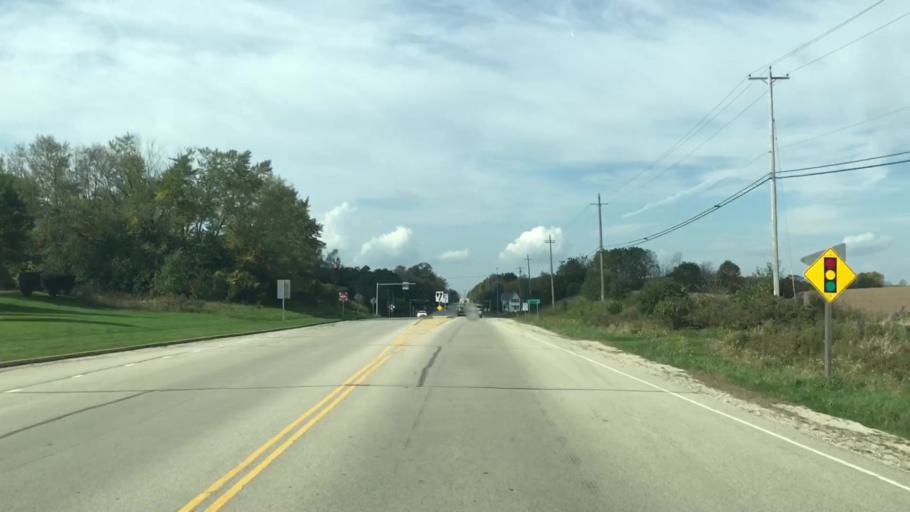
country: US
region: Wisconsin
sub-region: Ozaukee County
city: Mequon
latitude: 43.2214
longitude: -88.0400
